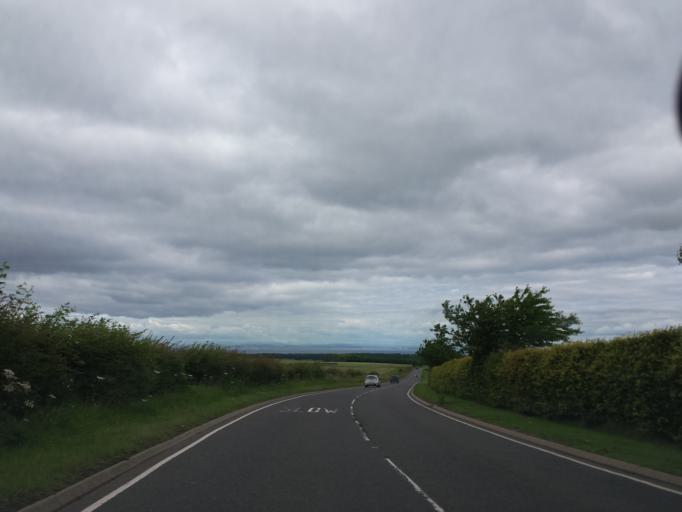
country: GB
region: Scotland
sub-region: East Lothian
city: Haddington
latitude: 55.9793
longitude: -2.8154
